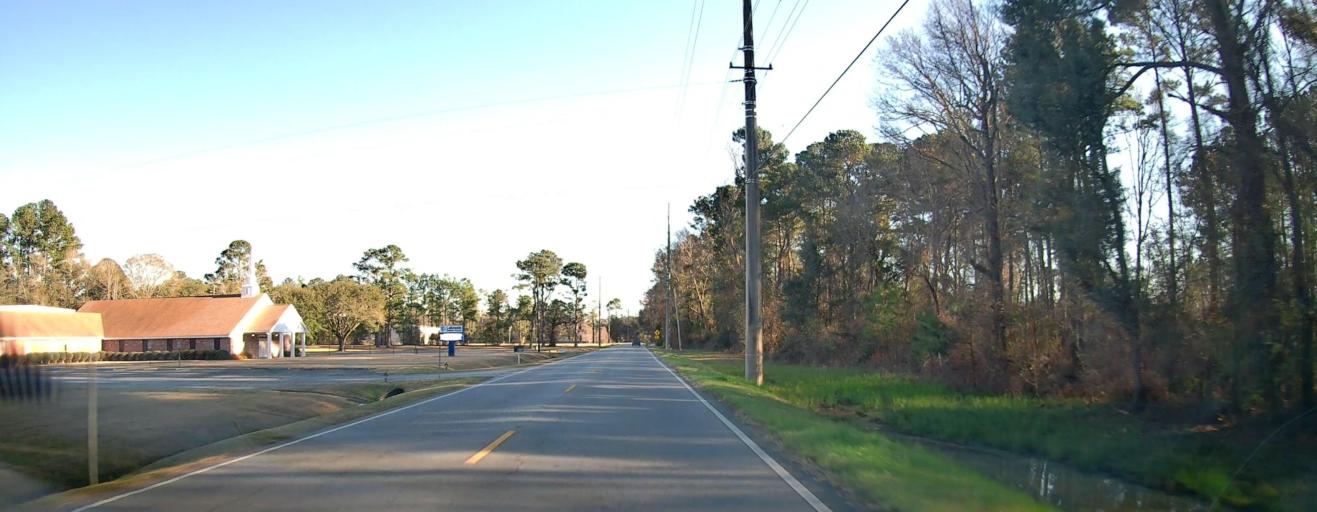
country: US
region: Georgia
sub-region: Dougherty County
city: Albany
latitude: 31.6187
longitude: -84.1610
